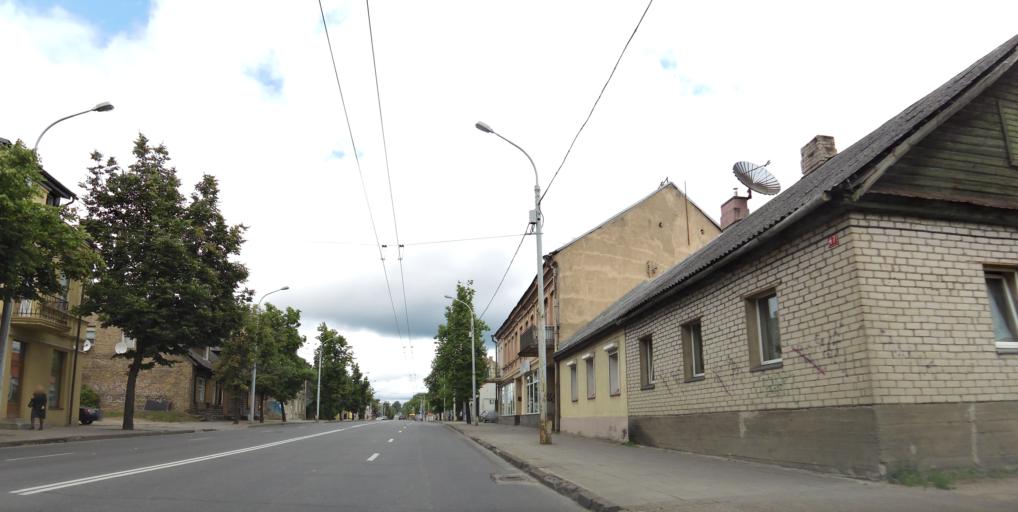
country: LT
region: Vilnius County
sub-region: Vilnius
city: Vilnius
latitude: 54.6978
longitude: 25.2822
